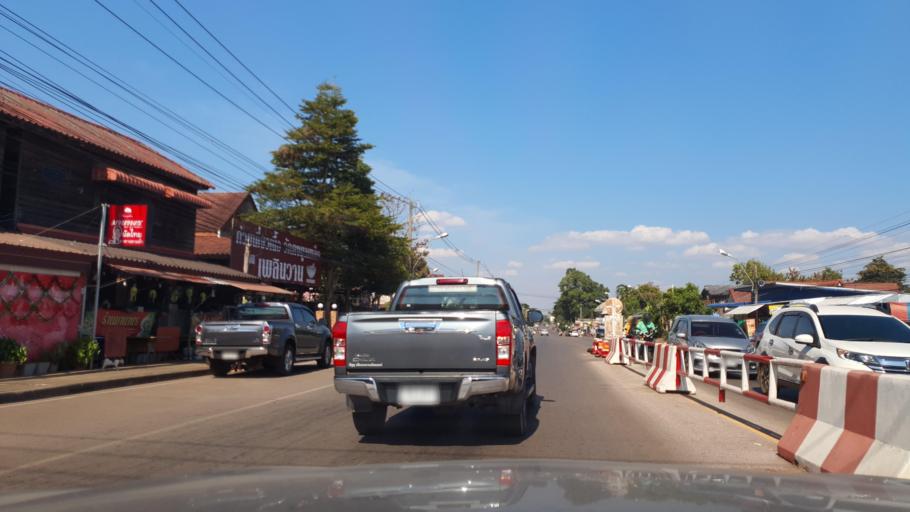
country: TH
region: Sakon Nakhon
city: Sakon Nakhon
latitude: 17.1643
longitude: 104.1235
